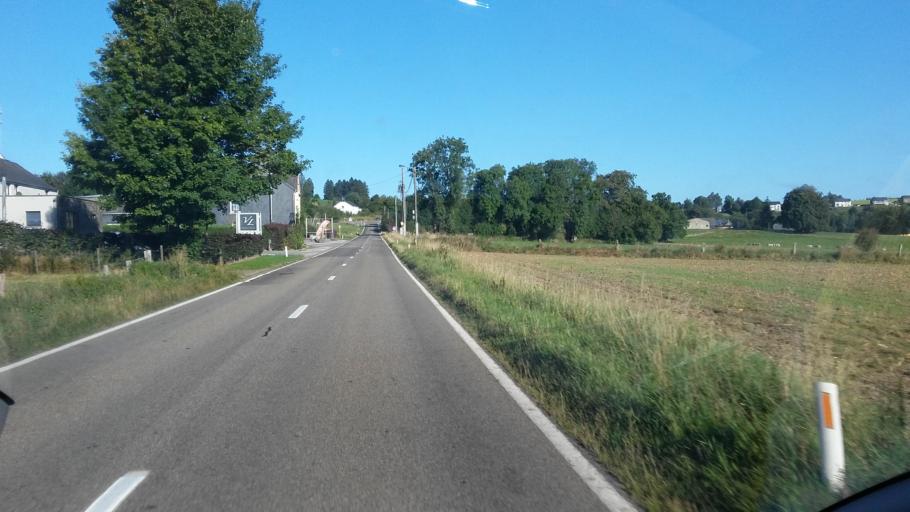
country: BE
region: Wallonia
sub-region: Province du Luxembourg
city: Neufchateau
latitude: 49.8289
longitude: 5.4831
